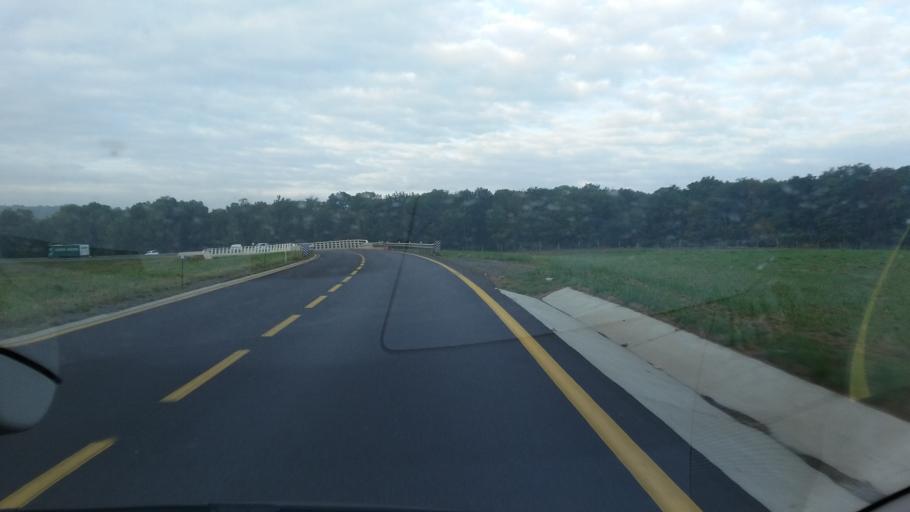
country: FR
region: Champagne-Ardenne
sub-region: Departement des Ardennes
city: La Francheville
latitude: 49.7201
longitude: 4.7018
